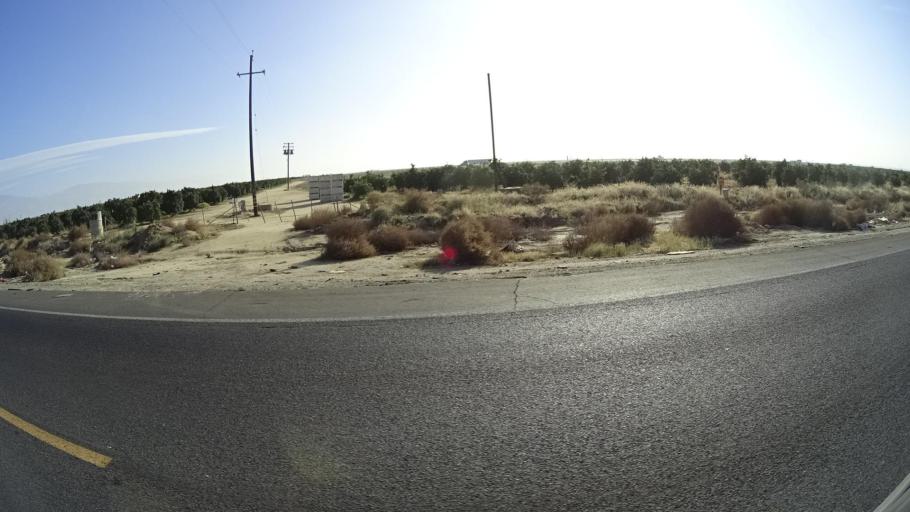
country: US
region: California
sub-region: Kern County
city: Lamont
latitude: 35.3390
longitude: -118.8341
